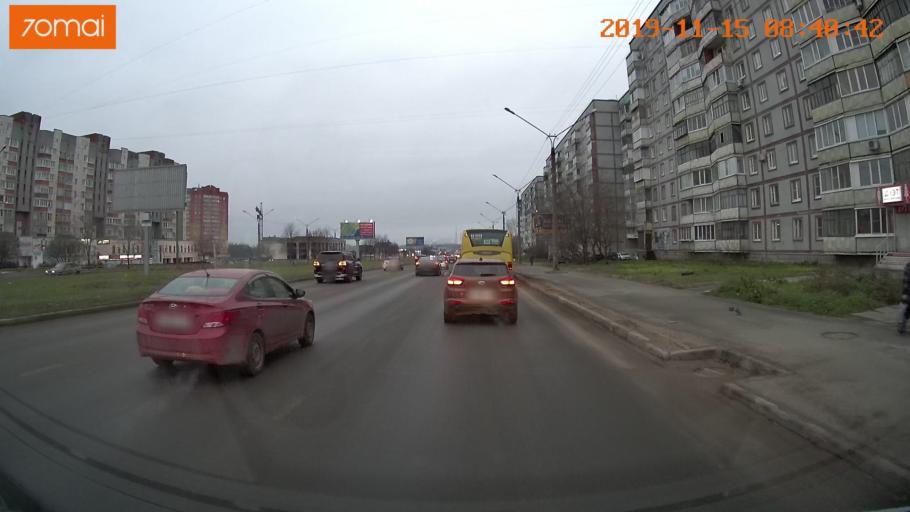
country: RU
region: Vologda
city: Cherepovets
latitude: 59.0952
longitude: 37.9137
